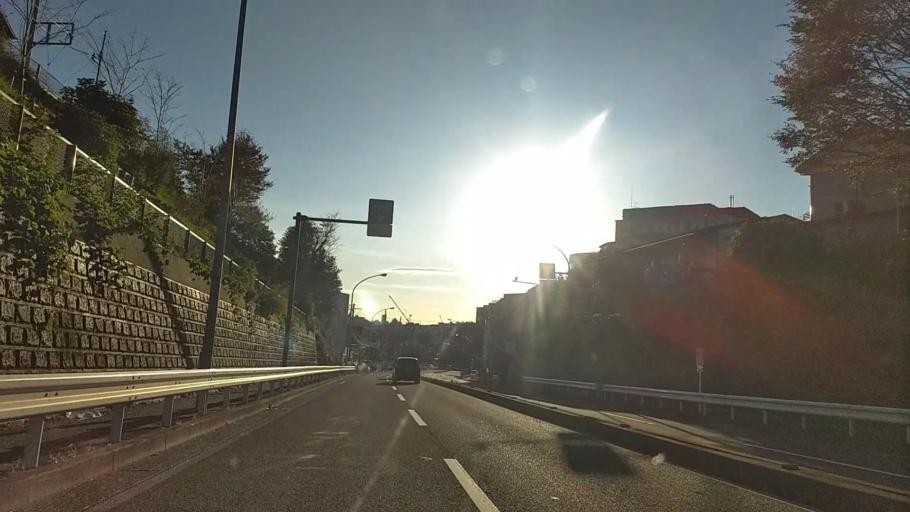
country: JP
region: Kanagawa
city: Yokohama
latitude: 35.4433
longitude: 139.6180
